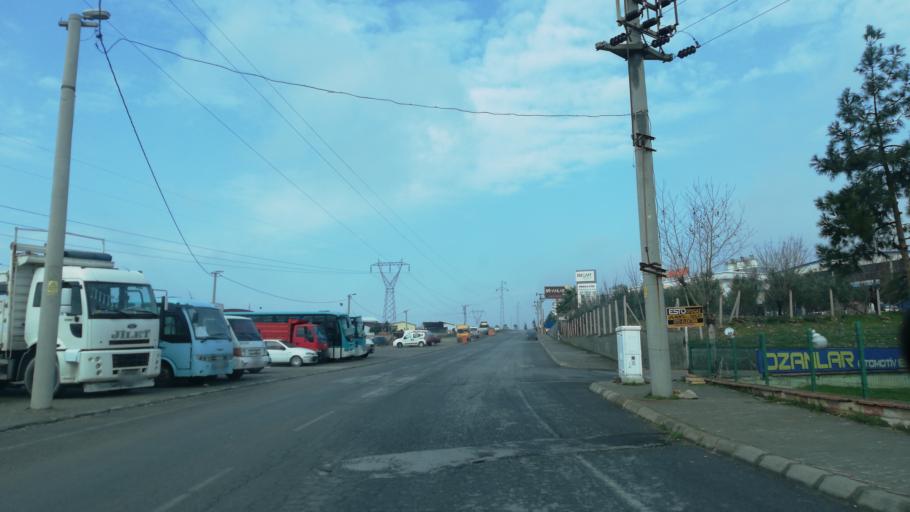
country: TR
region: Kahramanmaras
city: Kahramanmaras
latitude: 37.5635
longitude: 36.8925
